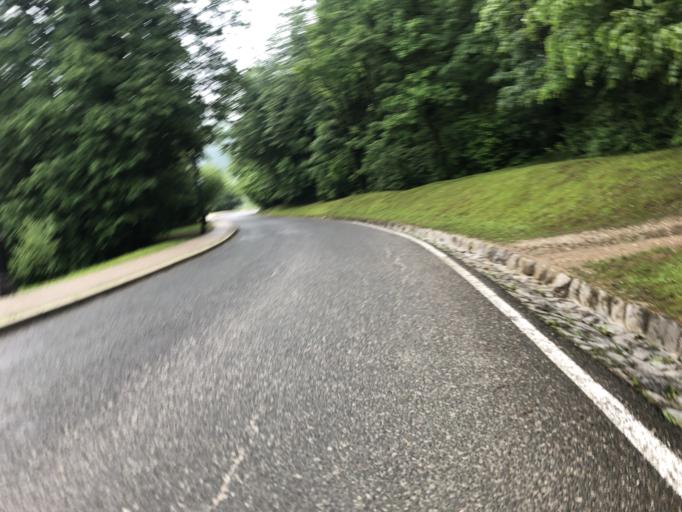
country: SI
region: Ljubljana
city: Ljubljana
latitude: 46.0457
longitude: 14.5133
